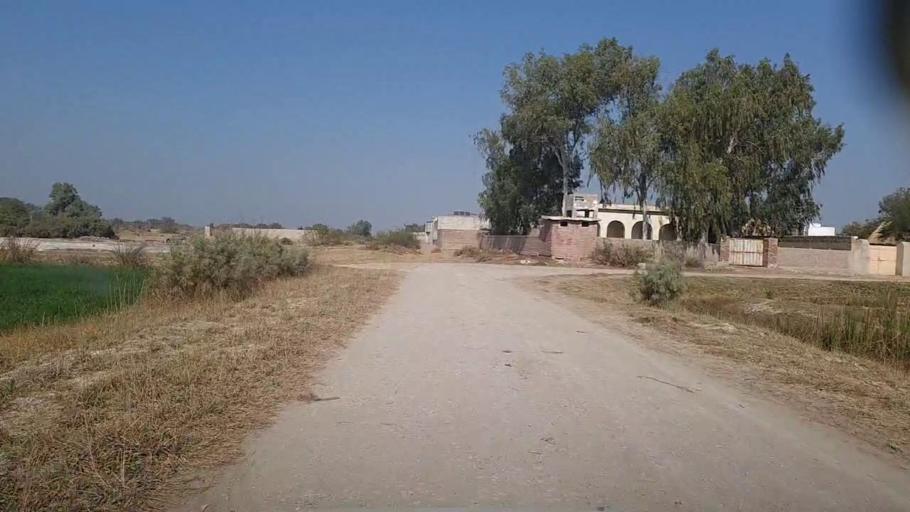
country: PK
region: Sindh
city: Khairpur
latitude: 27.9499
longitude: 69.7285
